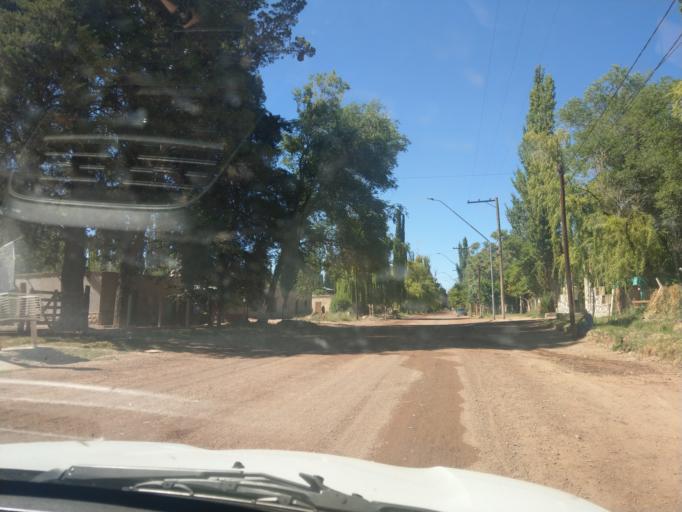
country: AR
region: San Juan
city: Tamberias
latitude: -31.6632
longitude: -69.4674
